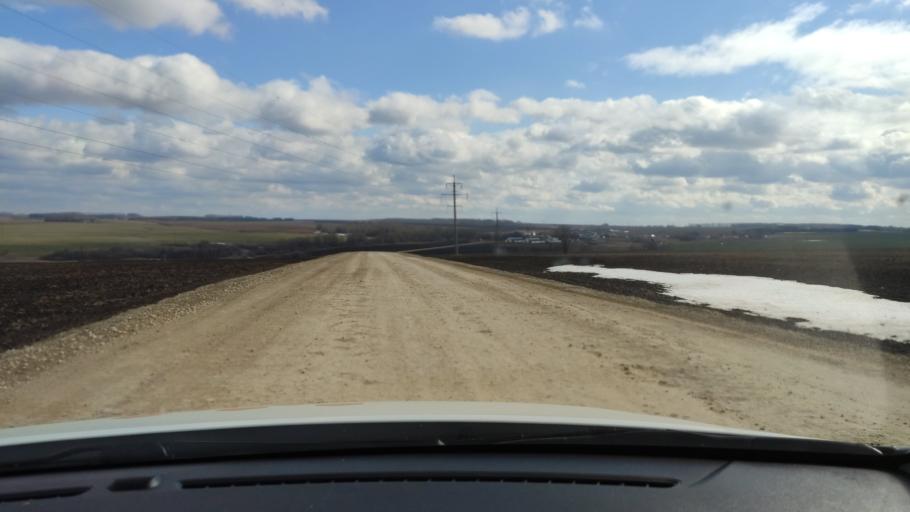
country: RU
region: Tatarstan
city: Vysokaya Gora
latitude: 56.2252
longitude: 49.3072
